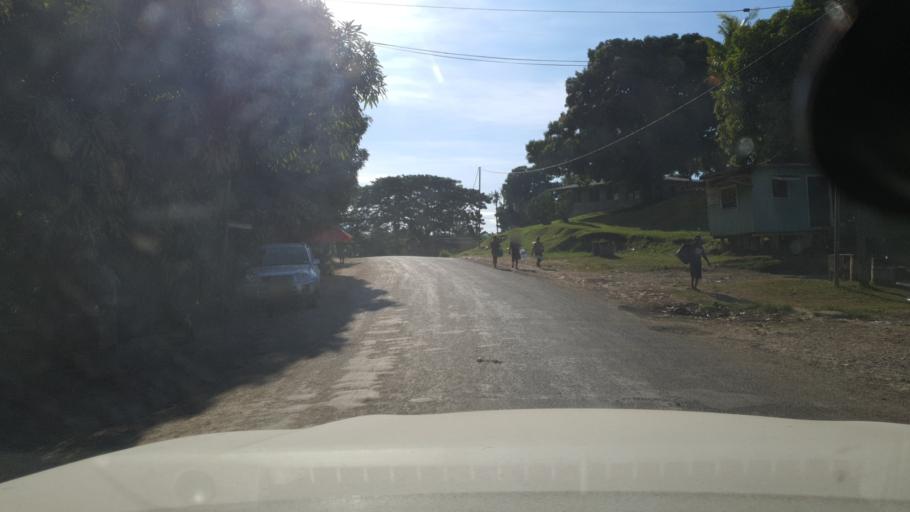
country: SB
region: Guadalcanal
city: Honiara
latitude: -9.4526
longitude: 159.9896
